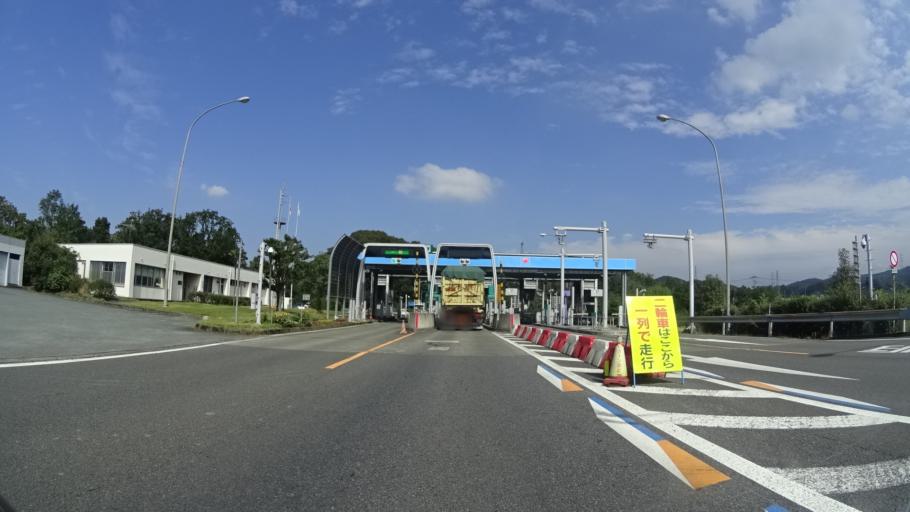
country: JP
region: Kumamoto
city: Matsubase
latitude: 32.6488
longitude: 130.7101
